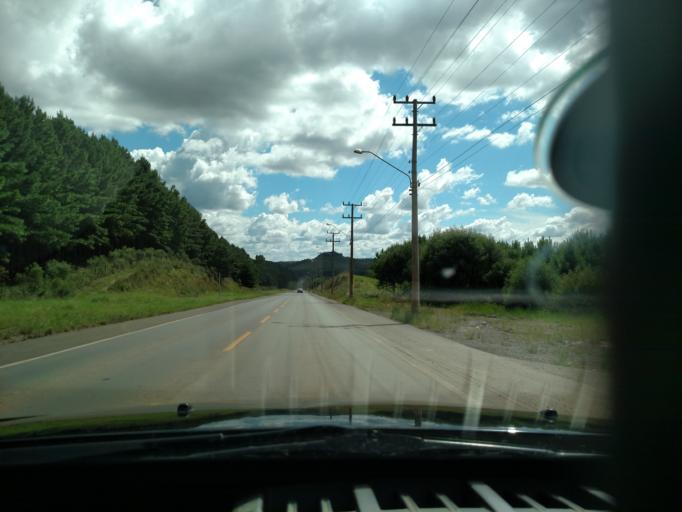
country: BR
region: Santa Catarina
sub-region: Lages
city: Lages
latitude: -27.8397
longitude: -50.3591
